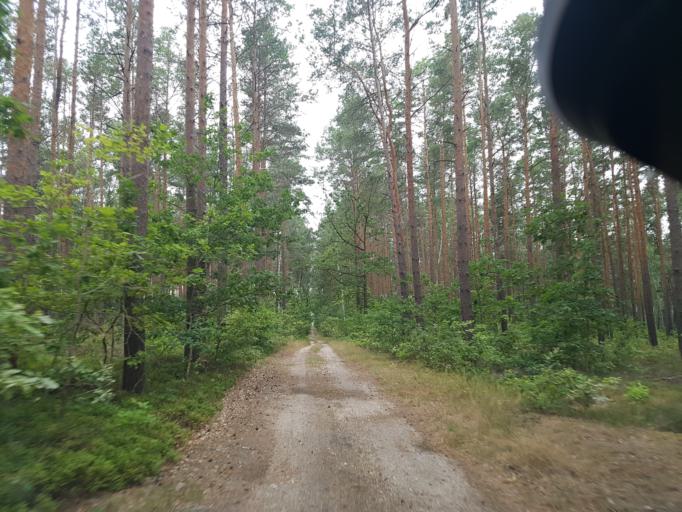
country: DE
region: Brandenburg
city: Ruckersdorf
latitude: 51.5966
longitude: 13.5701
